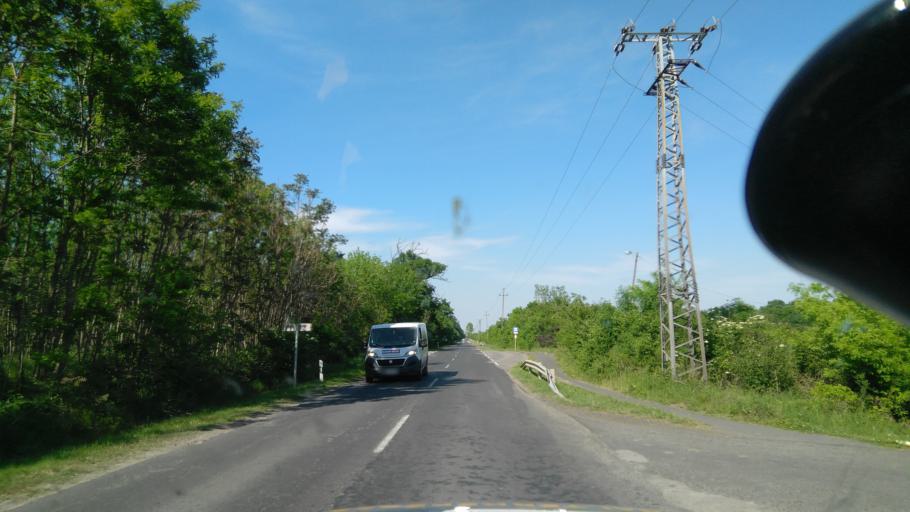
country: HU
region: Bekes
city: Gyula
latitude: 46.7042
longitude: 21.3154
